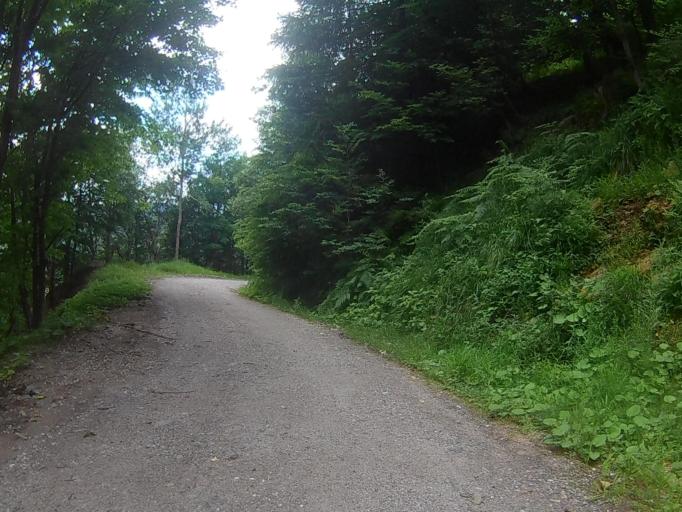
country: SI
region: Selnica ob Dravi
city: Selnica ob Dravi
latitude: 46.5073
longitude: 15.4658
